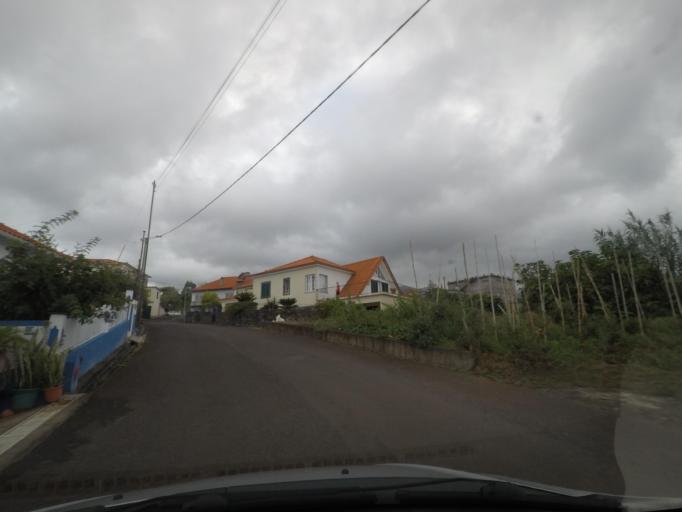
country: PT
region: Madeira
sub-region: Santana
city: Santana
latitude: 32.8134
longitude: -16.8853
